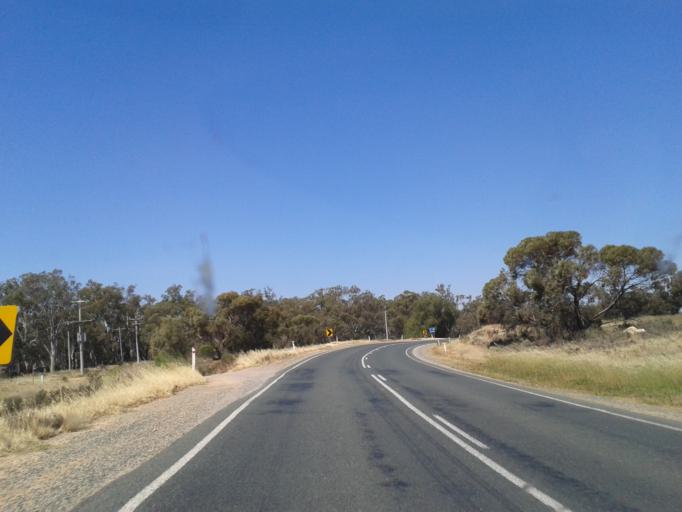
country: AU
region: Victoria
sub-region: Swan Hill
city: Swan Hill
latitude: -35.1000
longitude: 143.3421
